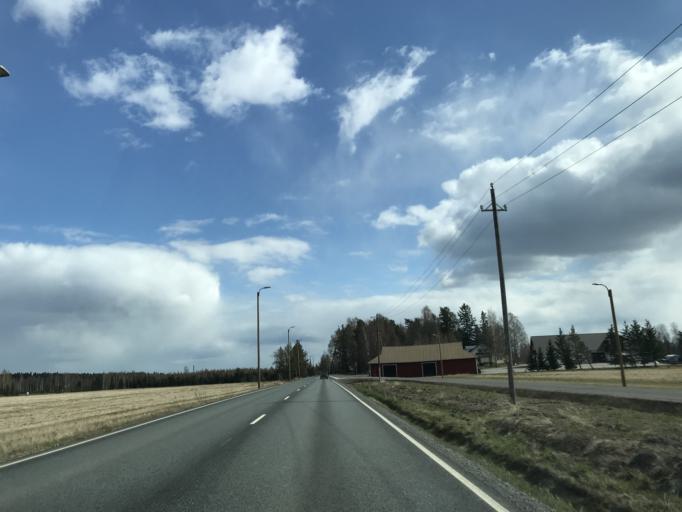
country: FI
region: Uusimaa
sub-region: Helsinki
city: Jaervenpaeae
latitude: 60.5127
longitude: 25.0269
